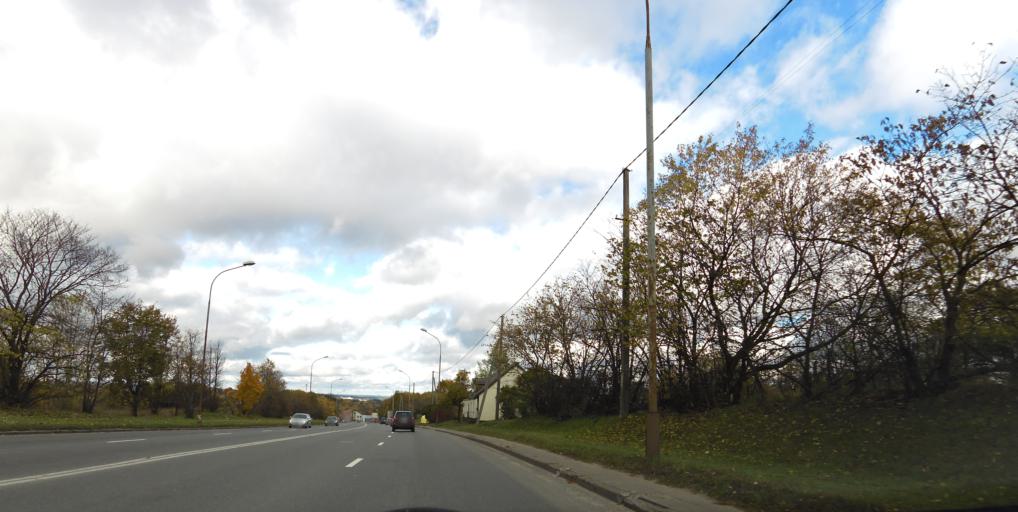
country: LT
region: Vilnius County
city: Rasos
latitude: 54.6569
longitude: 25.3033
